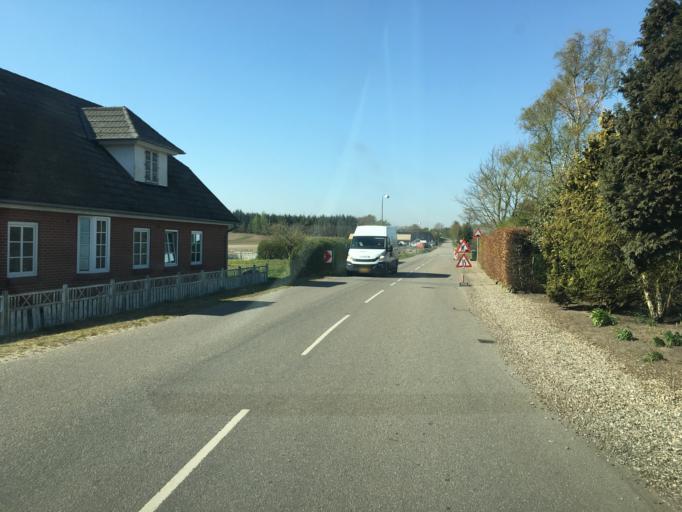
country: DK
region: South Denmark
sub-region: Aabenraa Kommune
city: Rodekro
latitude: 55.0895
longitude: 9.2745
